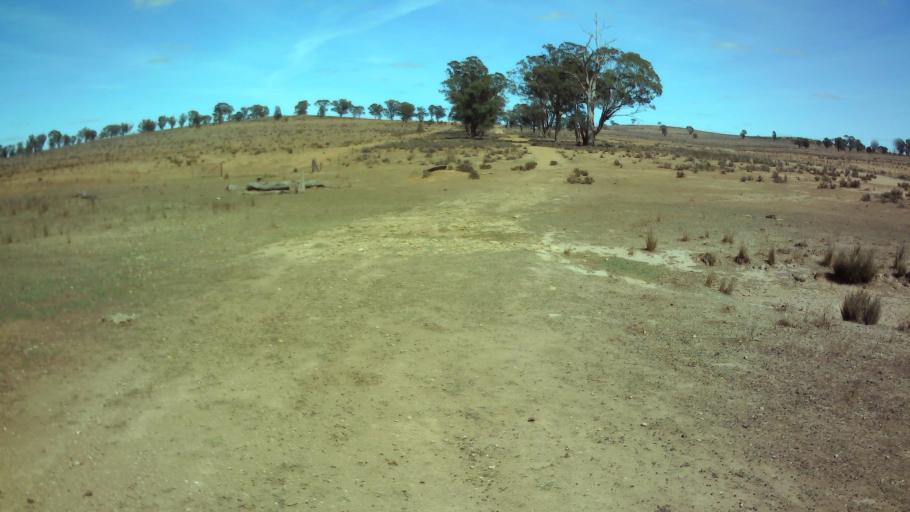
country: AU
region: New South Wales
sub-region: Weddin
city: Grenfell
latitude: -33.7212
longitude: 147.8430
